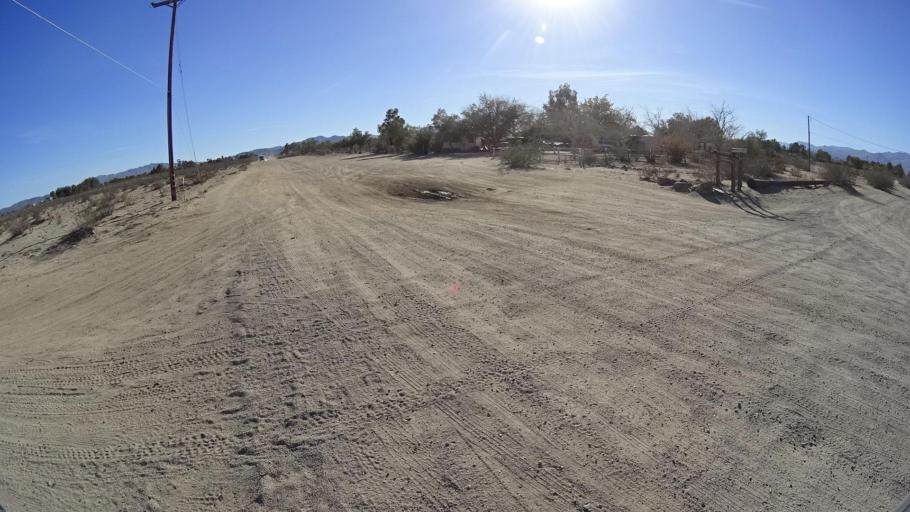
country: US
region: California
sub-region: Kern County
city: China Lake Acres
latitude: 35.6376
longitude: -117.7675
